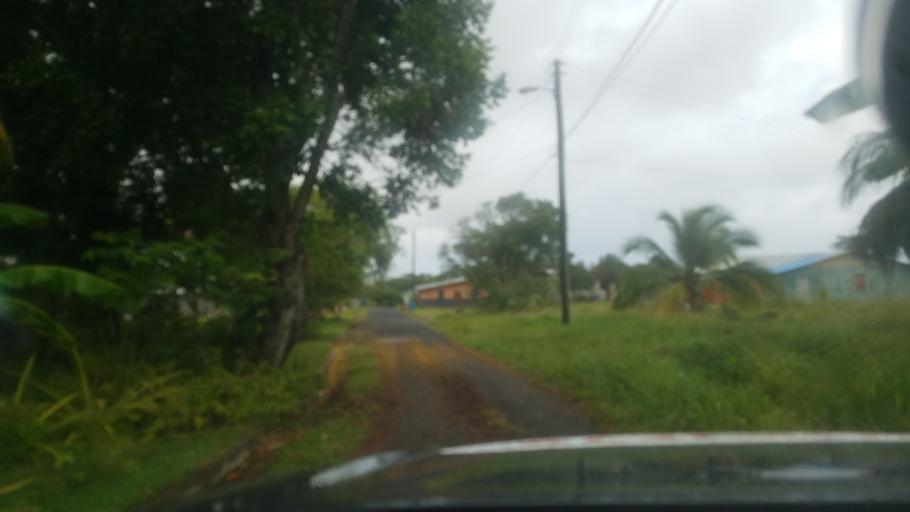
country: LC
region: Laborie Quarter
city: Laborie
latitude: 13.7675
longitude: -60.9727
